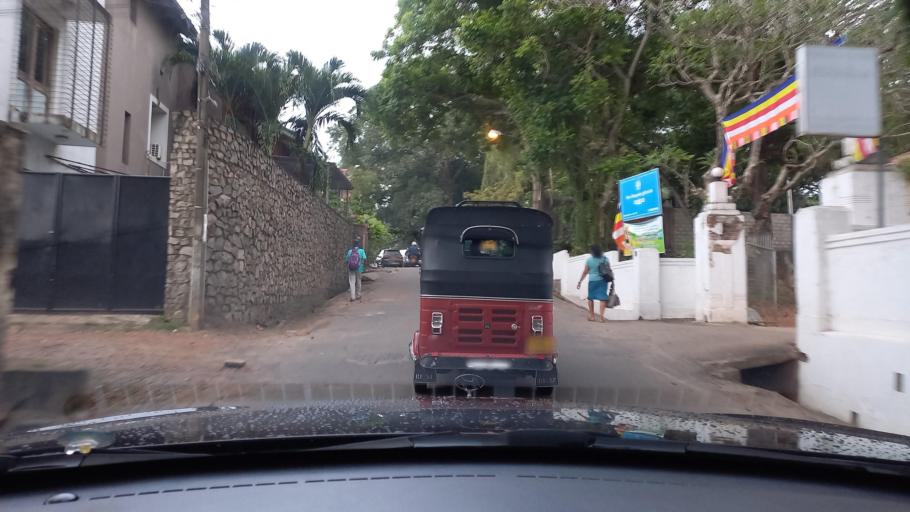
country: LK
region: Western
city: Pita Kotte
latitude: 6.8772
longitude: 79.8819
